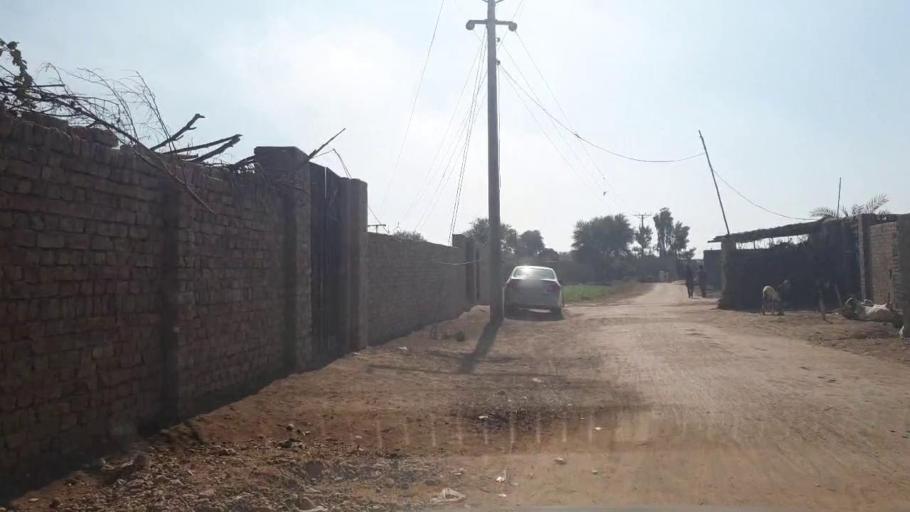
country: PK
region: Sindh
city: Shahdadpur
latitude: 25.9152
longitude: 68.5778
